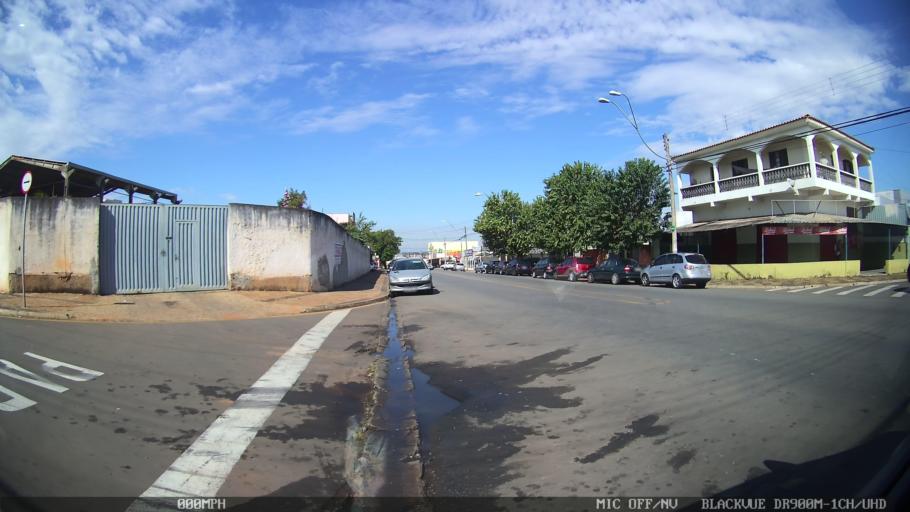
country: BR
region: Sao Paulo
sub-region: Americana
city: Americana
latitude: -22.7456
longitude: -47.3700
